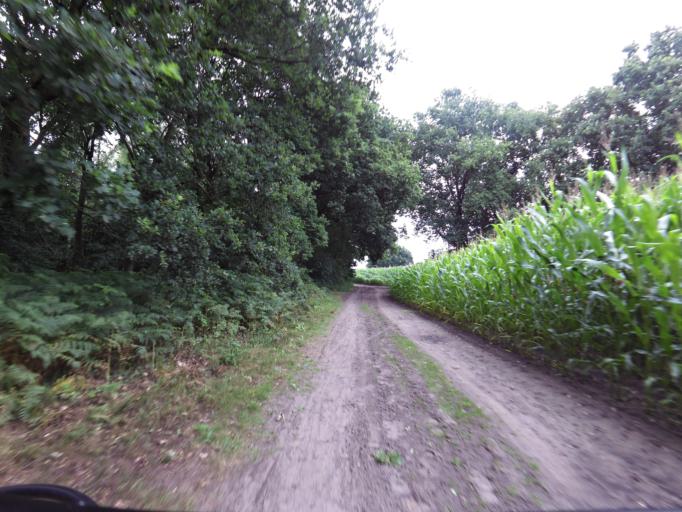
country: NL
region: North Brabant
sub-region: Gemeente Son en Breugel
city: Breugel
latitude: 51.5387
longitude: 5.4978
